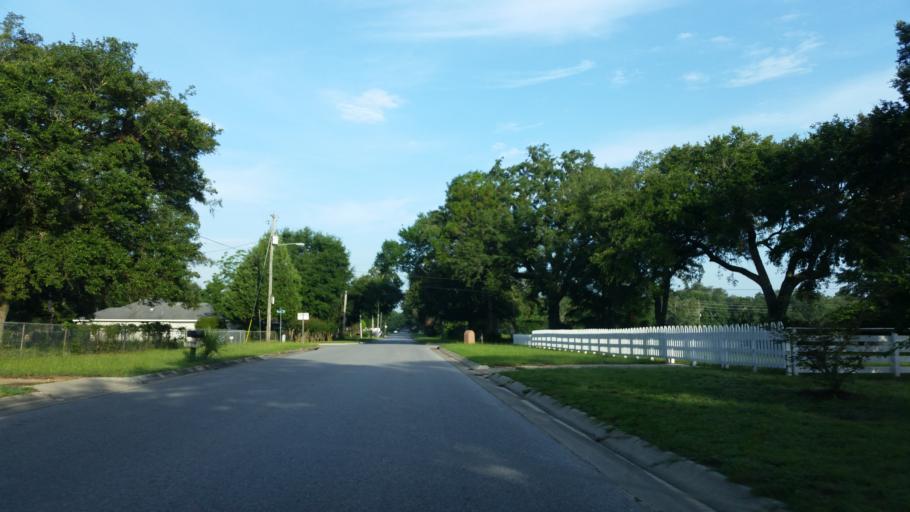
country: US
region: Florida
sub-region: Escambia County
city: Ferry Pass
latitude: 30.4918
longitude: -87.2022
